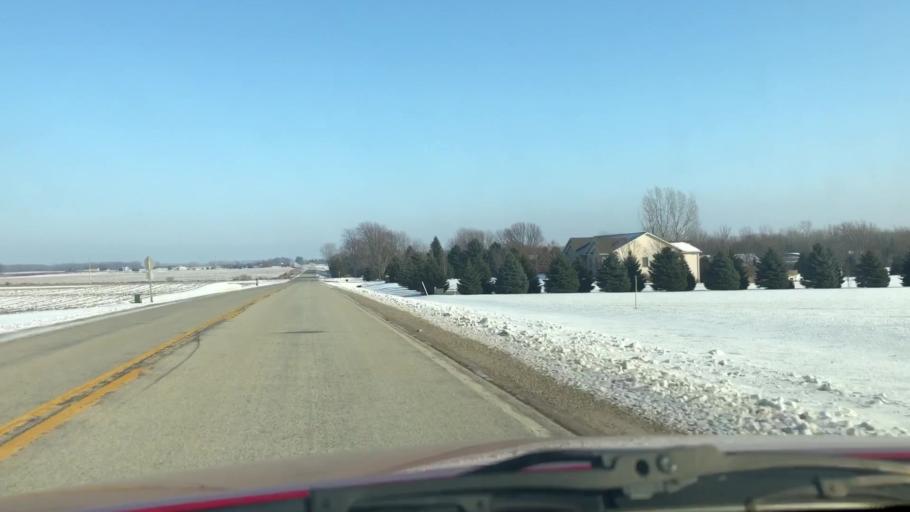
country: US
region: Wisconsin
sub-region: Outagamie County
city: Seymour
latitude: 44.4436
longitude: -88.3546
